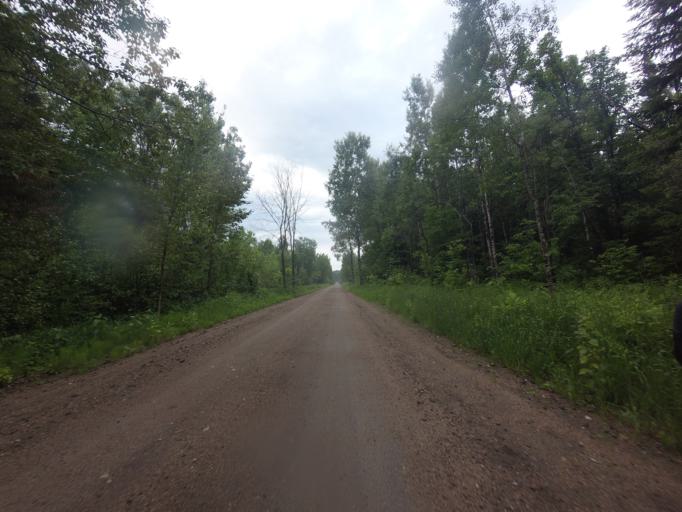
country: CA
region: Quebec
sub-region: Outaouais
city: Maniwaki
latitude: 46.3372
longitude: -76.0029
